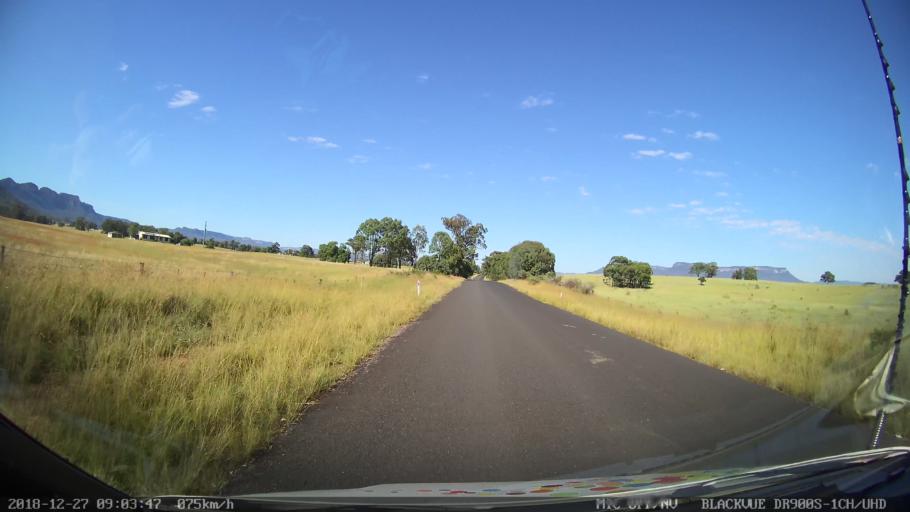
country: AU
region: New South Wales
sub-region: Lithgow
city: Portland
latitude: -33.1068
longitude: 150.1978
